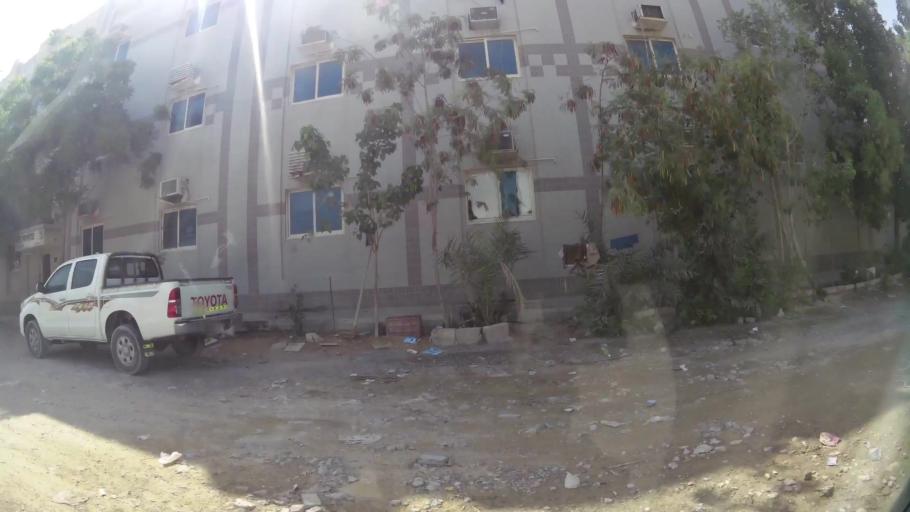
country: AE
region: Ash Shariqah
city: Sharjah
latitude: 25.3107
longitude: 55.3831
